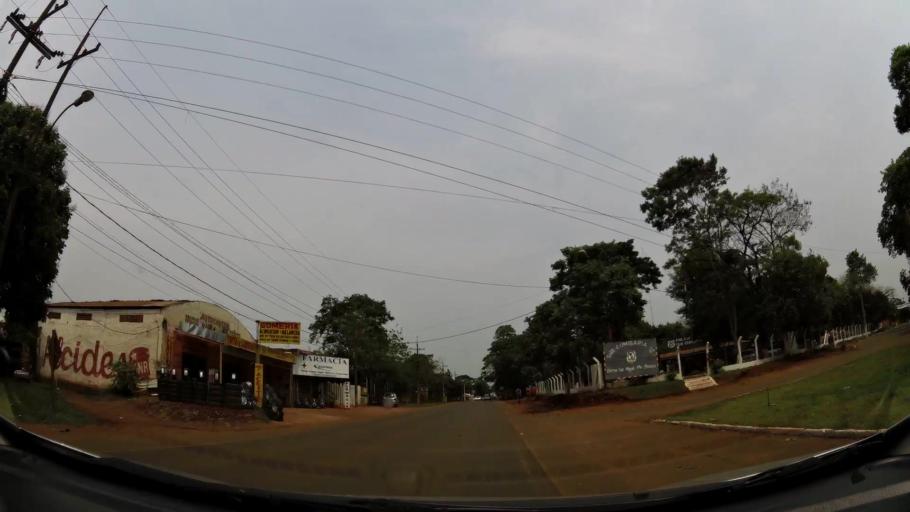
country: PY
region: Alto Parana
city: Presidente Franco
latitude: -25.5529
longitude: -54.6400
